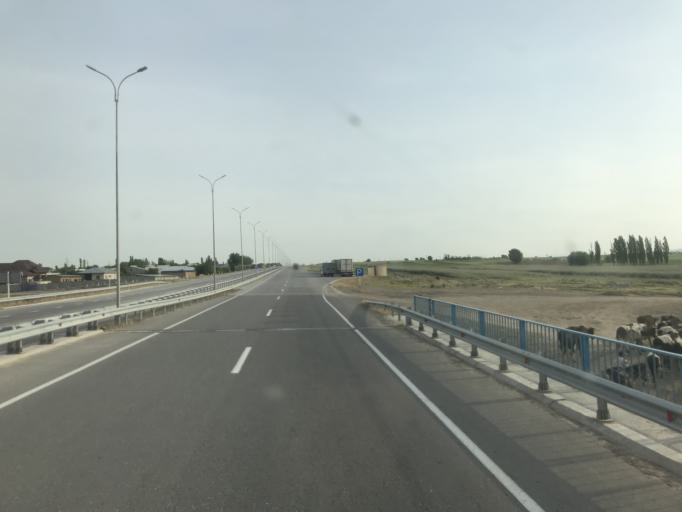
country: UZ
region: Toshkent
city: Qibray
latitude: 41.5546
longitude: 69.4077
